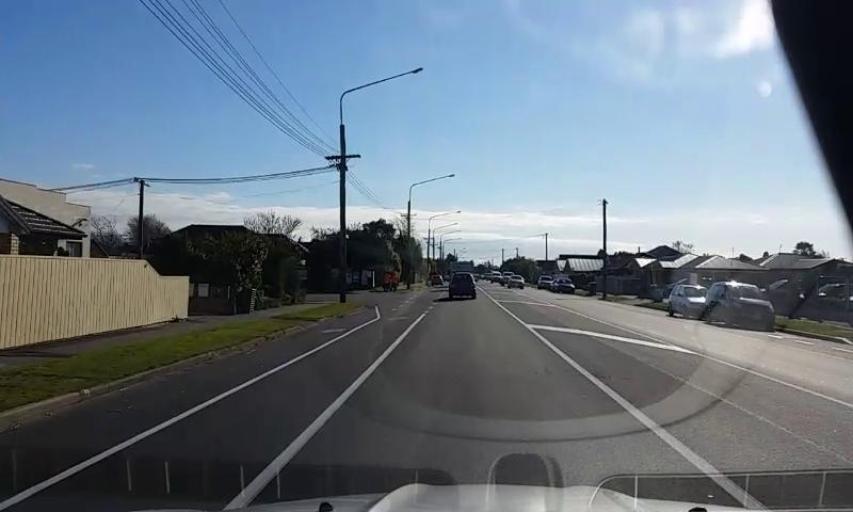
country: NZ
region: Canterbury
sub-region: Christchurch City
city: Christchurch
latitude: -43.5034
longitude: 172.6623
